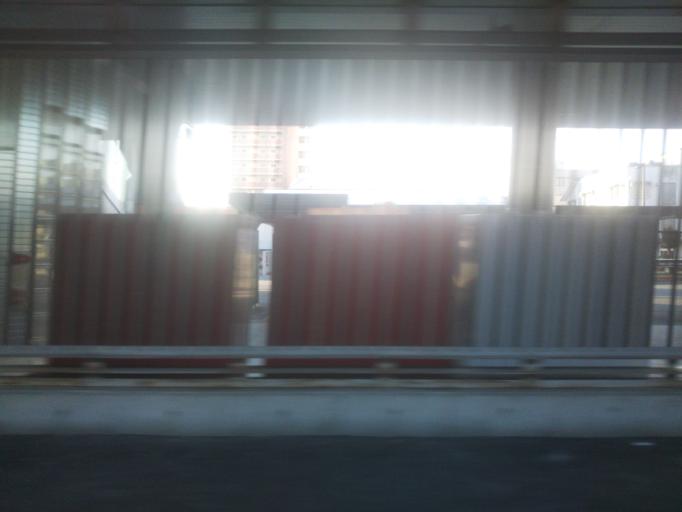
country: JP
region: Shiga Prefecture
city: Kusatsu
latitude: 35.0273
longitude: 135.9996
